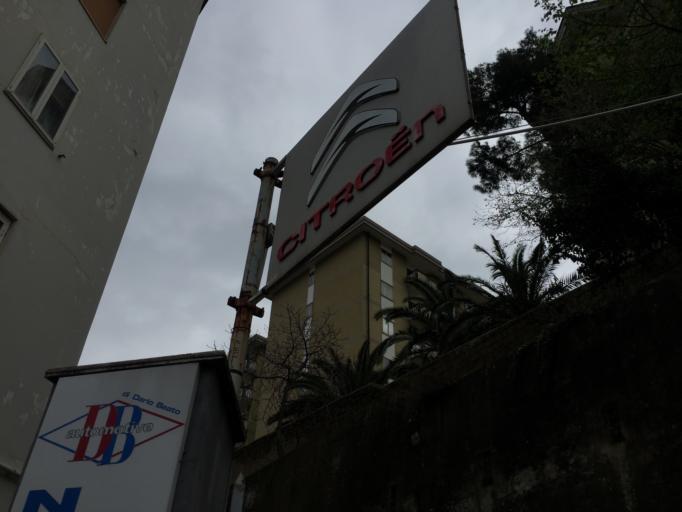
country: IT
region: Campania
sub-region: Provincia di Napoli
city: Napoli
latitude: 40.8584
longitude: 14.2276
